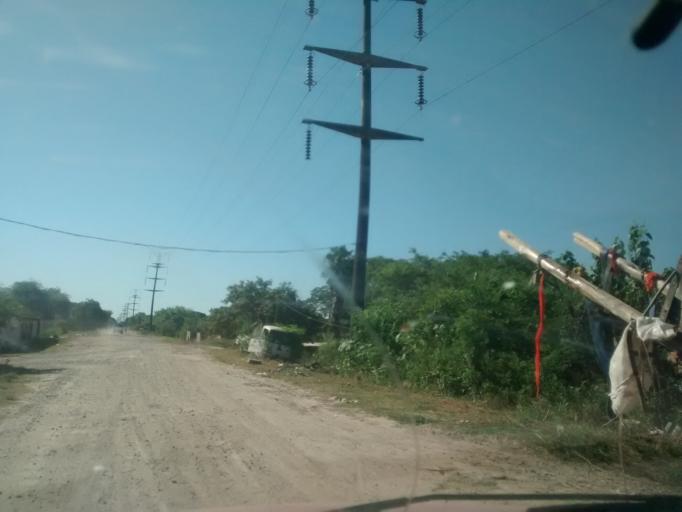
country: AR
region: Chaco
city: Resistencia
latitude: -27.4361
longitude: -58.9605
